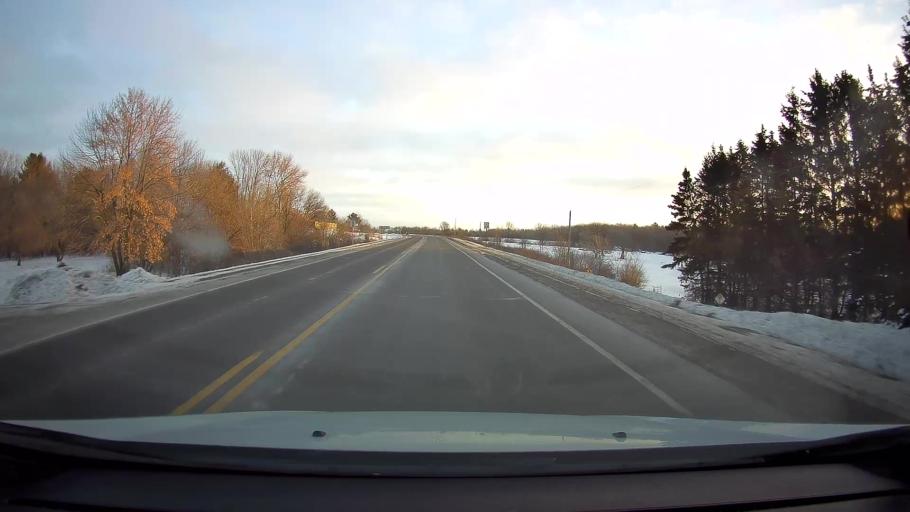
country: US
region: Wisconsin
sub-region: Polk County
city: Clear Lake
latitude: 45.2565
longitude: -92.2688
